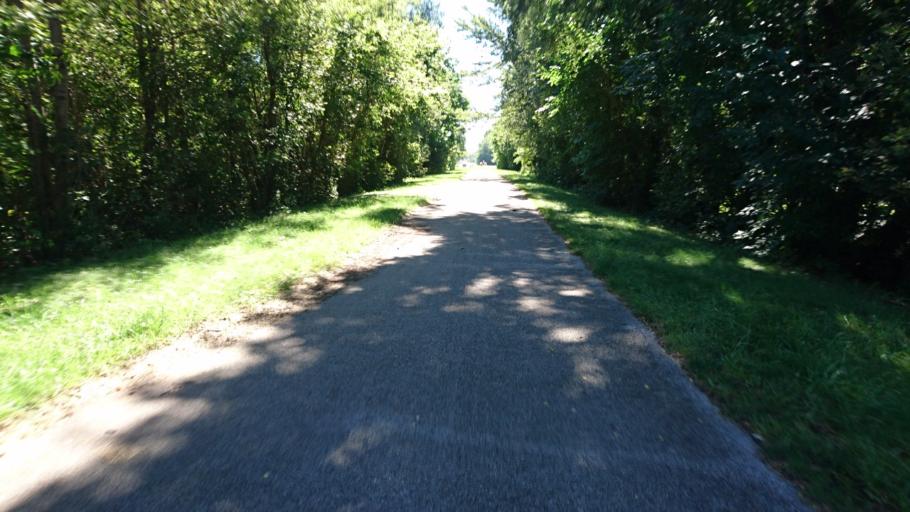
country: US
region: Illinois
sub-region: Cook County
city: Lansing
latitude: 41.5695
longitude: -87.5391
